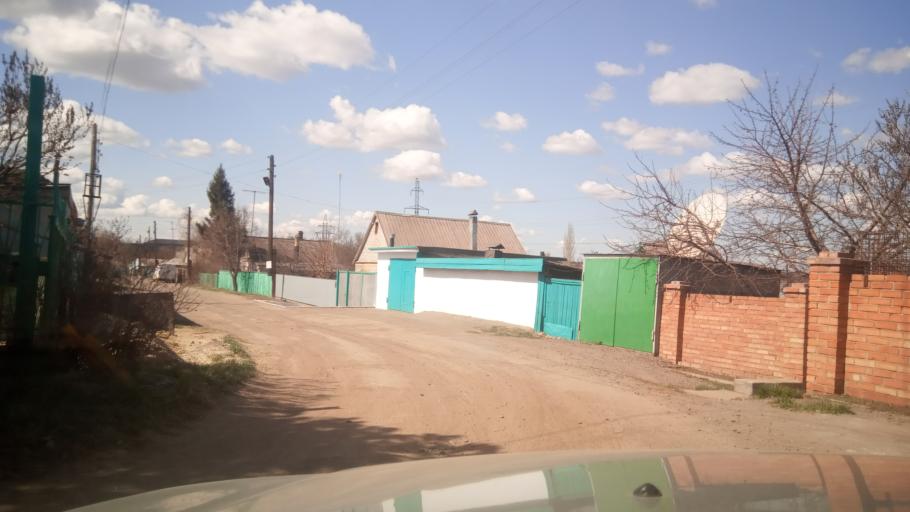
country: RU
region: Orenburg
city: Novotroitsk
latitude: 51.2095
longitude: 58.3153
